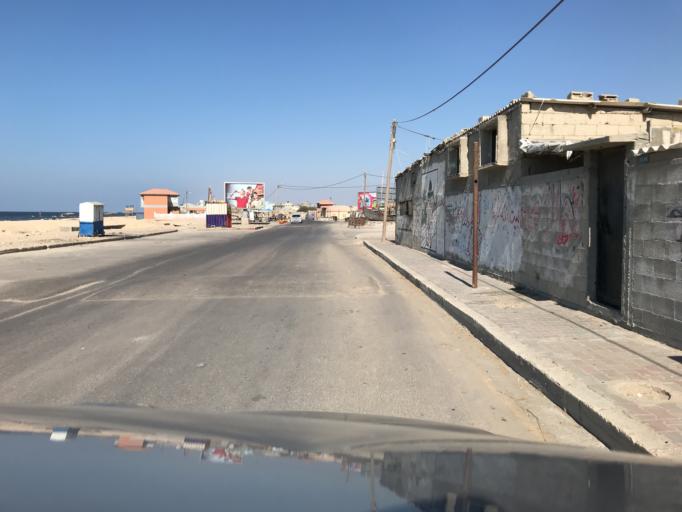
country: PS
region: Gaza Strip
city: Dayr al Balah
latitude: 31.4291
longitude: 34.3423
